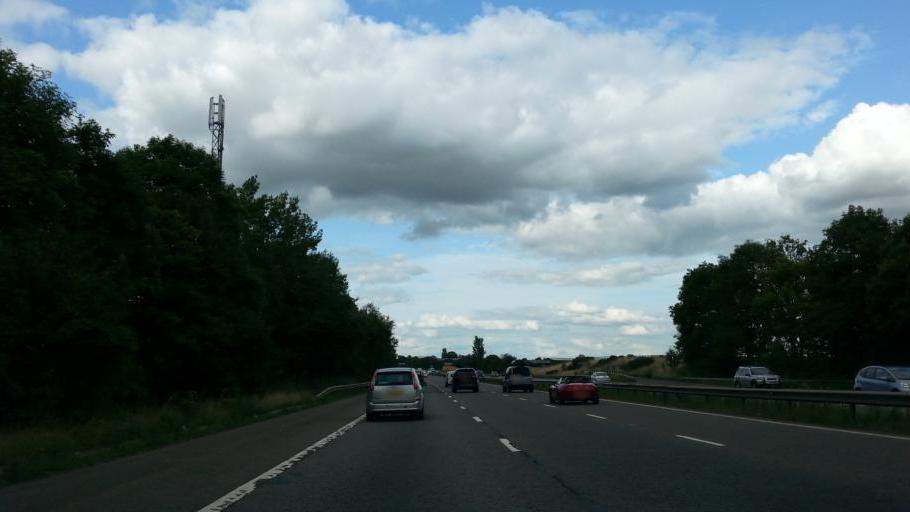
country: GB
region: England
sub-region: Warwickshire
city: Bedworth
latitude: 52.4654
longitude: -1.4097
